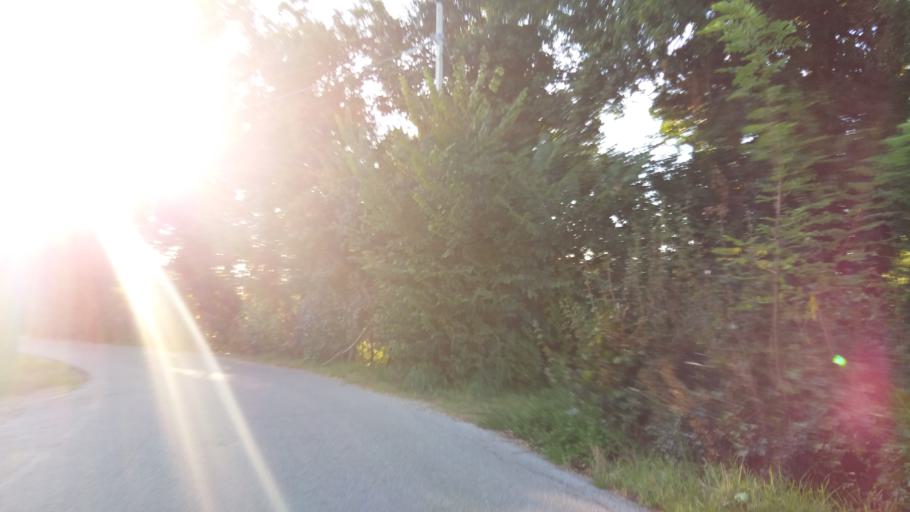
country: IT
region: Piedmont
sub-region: Provincia di Asti
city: Asti
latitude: 44.9245
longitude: 8.1896
